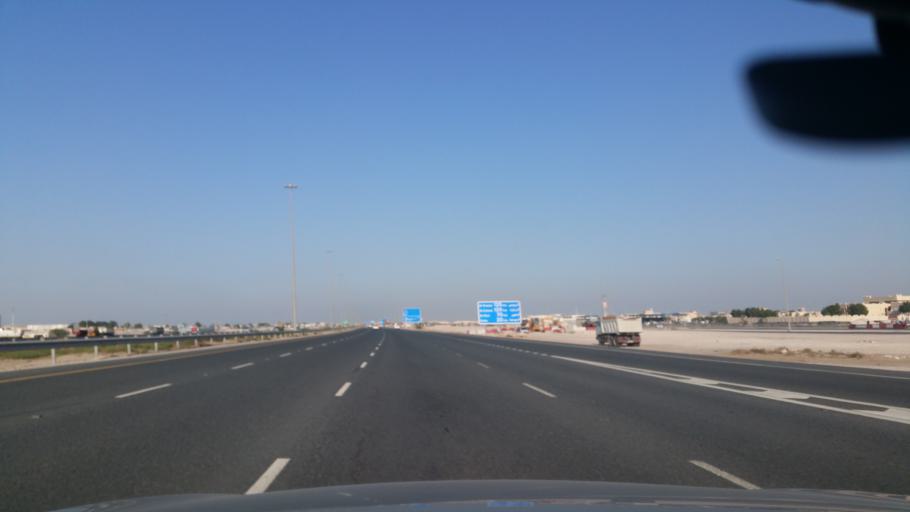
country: QA
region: Baladiyat ar Rayyan
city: Ar Rayyan
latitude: 25.1872
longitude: 51.3654
